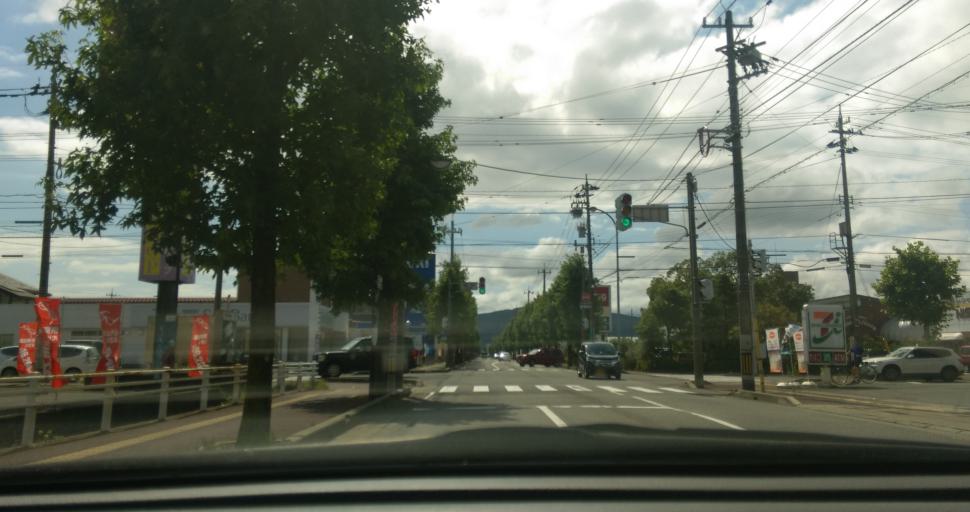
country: JP
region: Fukui
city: Fukui-shi
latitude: 36.0878
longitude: 136.2213
